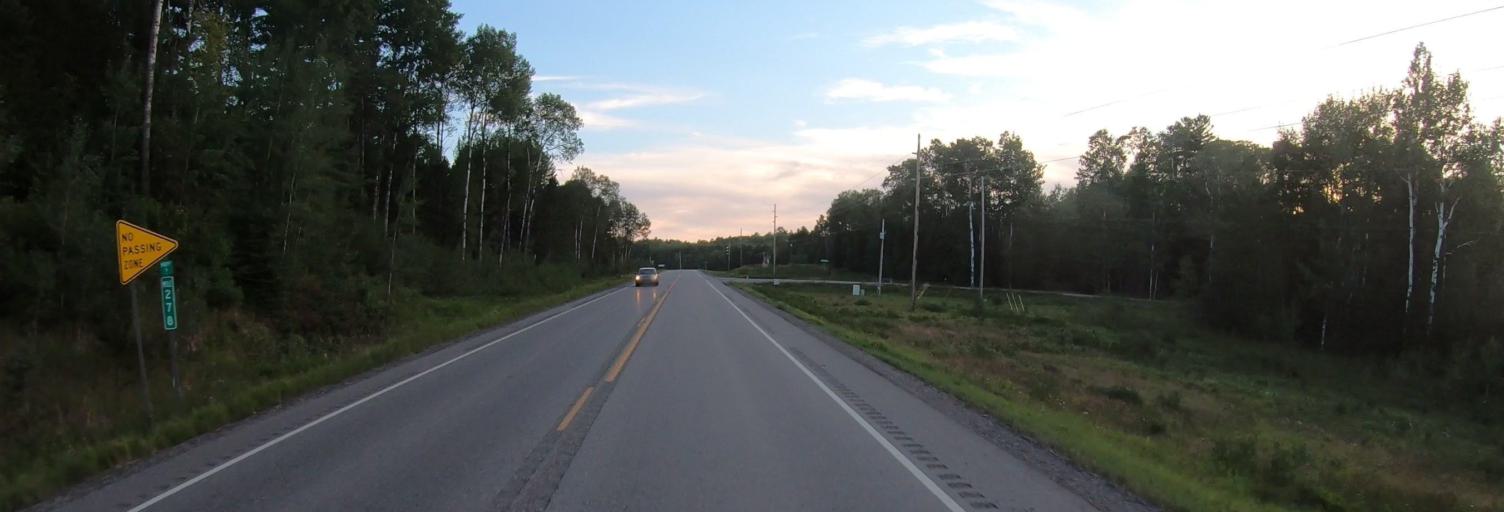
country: US
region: Minnesota
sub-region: Saint Louis County
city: Ely
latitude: 47.8816
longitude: -92.0056
